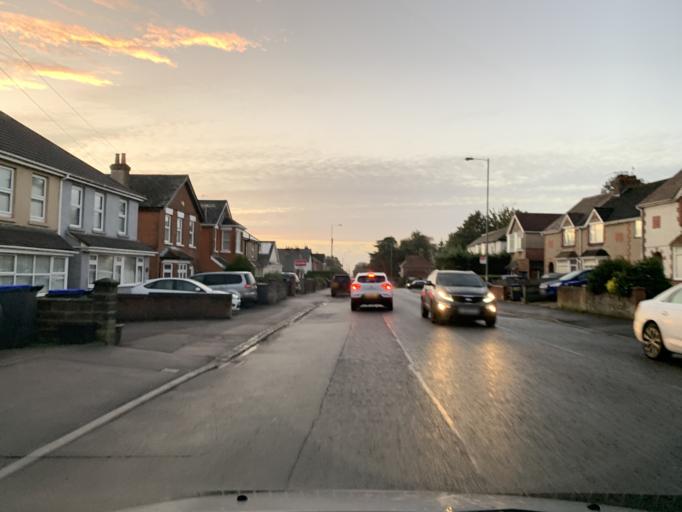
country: GB
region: England
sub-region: Wiltshire
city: Salisbury
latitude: 51.0812
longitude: -1.8176
